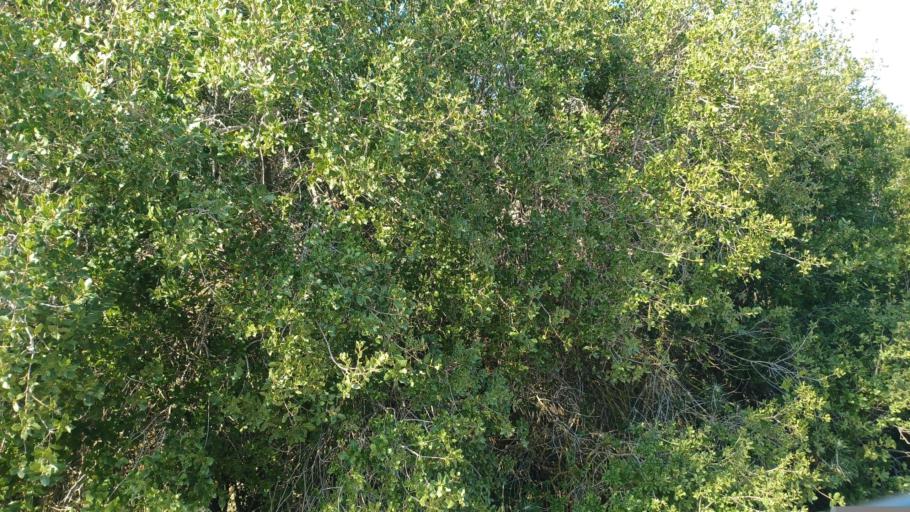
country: CY
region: Pafos
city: Mesogi
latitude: 34.8507
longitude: 32.5122
